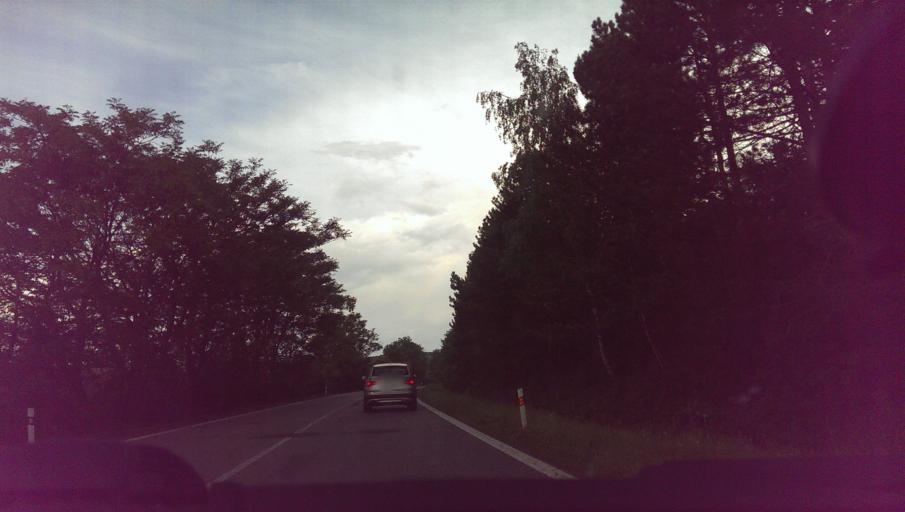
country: CZ
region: Zlin
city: Korycany
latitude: 49.1582
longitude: 17.1440
